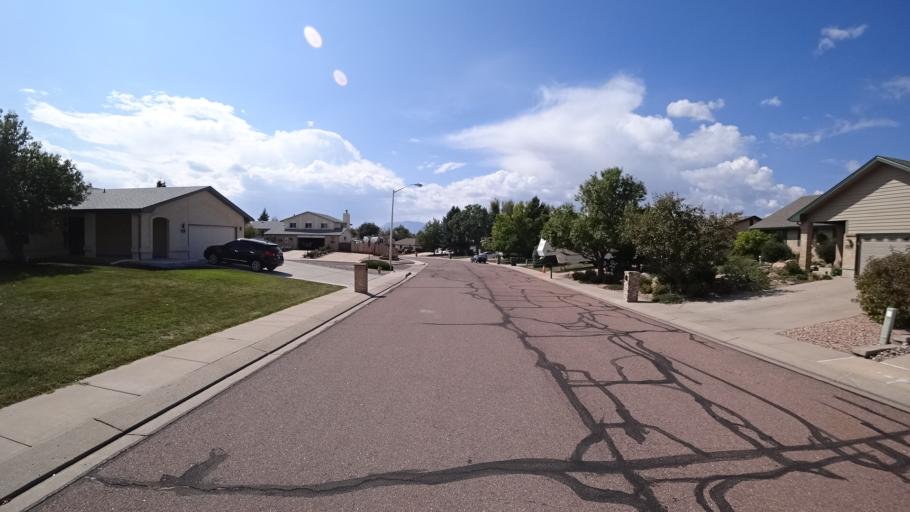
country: US
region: Colorado
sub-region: El Paso County
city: Cimarron Hills
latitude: 38.8636
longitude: -104.7282
